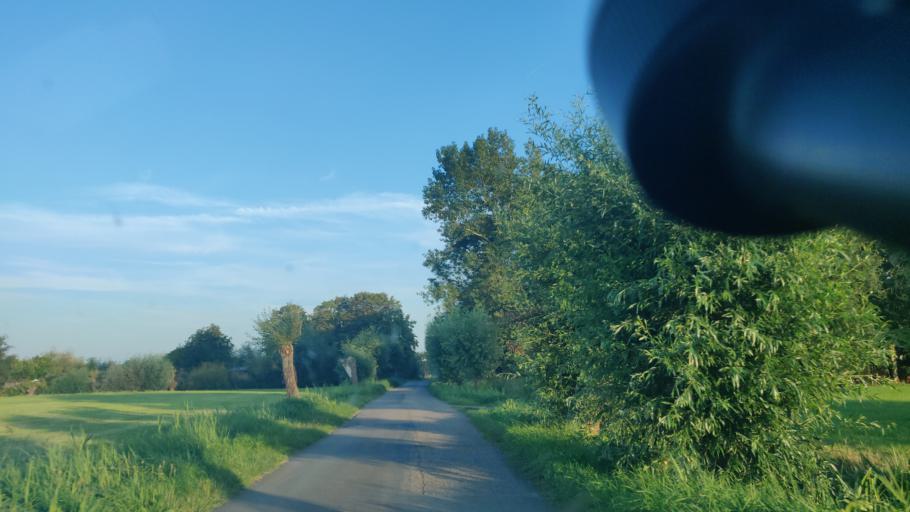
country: NL
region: South Holland
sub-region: Gemeente Voorschoten
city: Voorschoten
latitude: 52.1444
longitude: 4.4399
